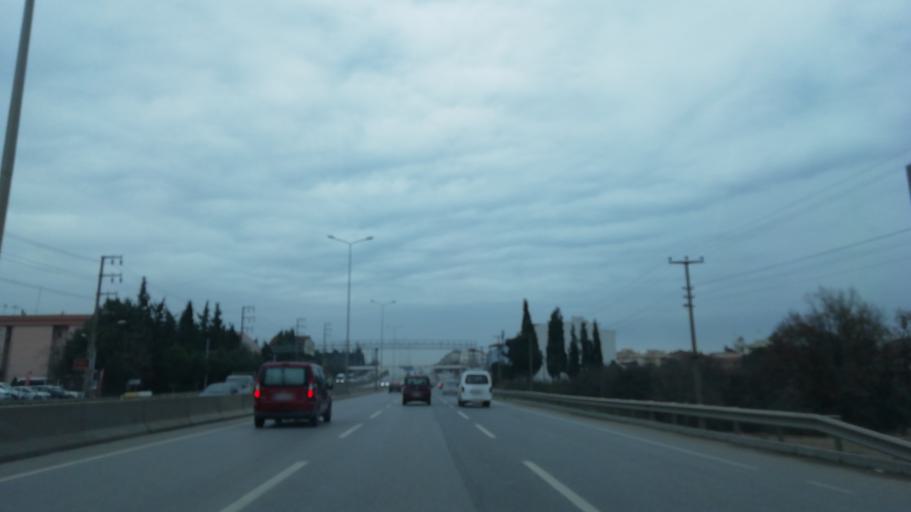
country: TR
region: Kocaeli
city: Derince
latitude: 40.7571
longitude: 29.8052
